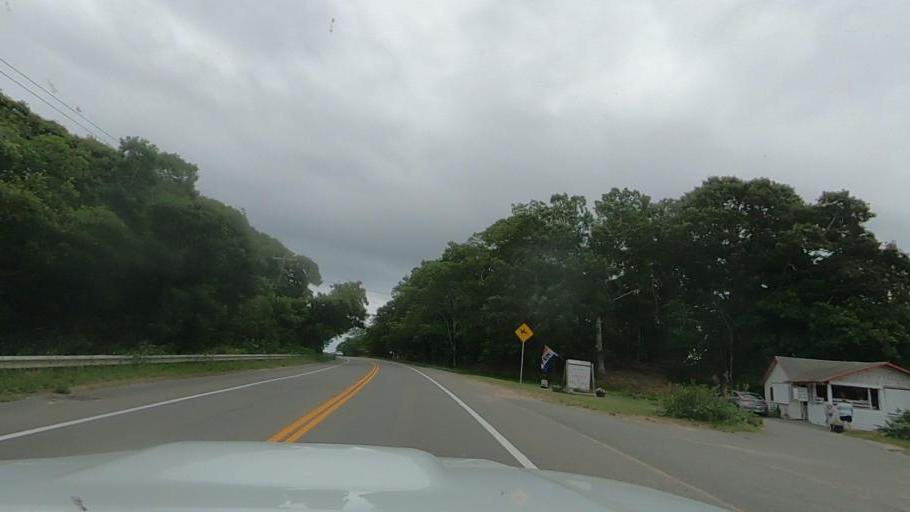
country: US
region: Massachusetts
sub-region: Barnstable County
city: Wellfleet
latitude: 41.9454
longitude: -70.0311
